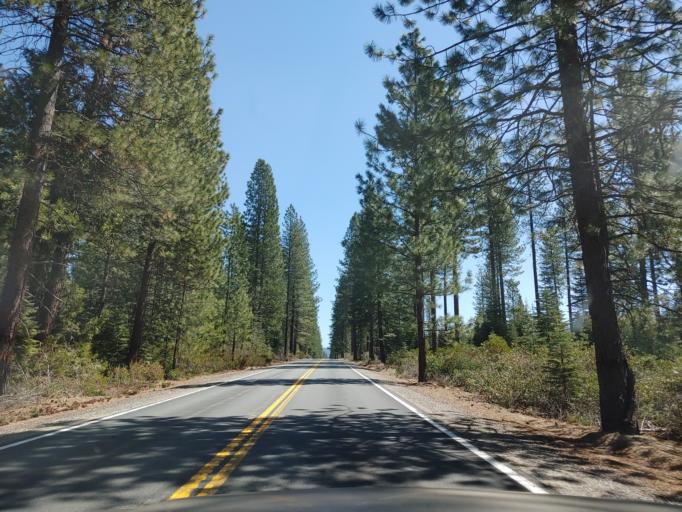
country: US
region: California
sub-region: Siskiyou County
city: McCloud
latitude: 41.2665
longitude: -121.8732
